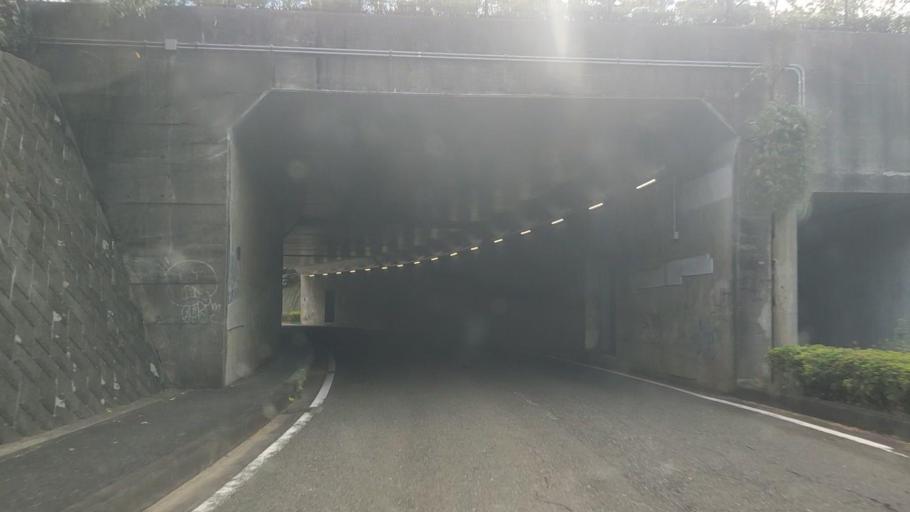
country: JP
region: Kanagawa
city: Yokohama
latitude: 35.4460
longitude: 139.5497
